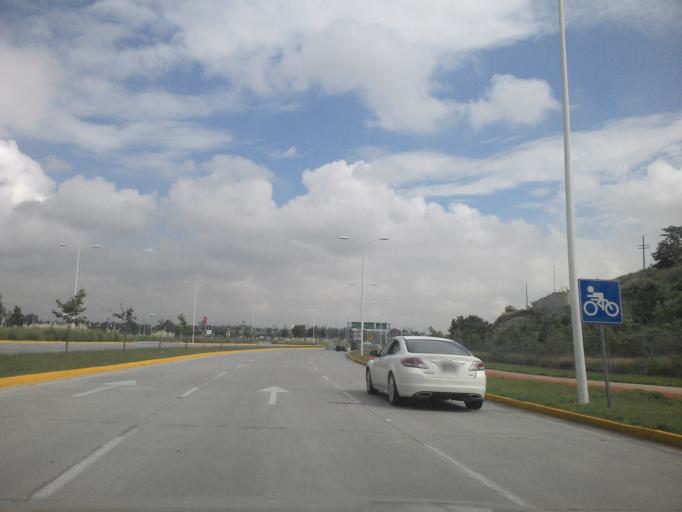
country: MX
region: Jalisco
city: Zapopan2
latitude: 20.6823
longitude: -103.4605
